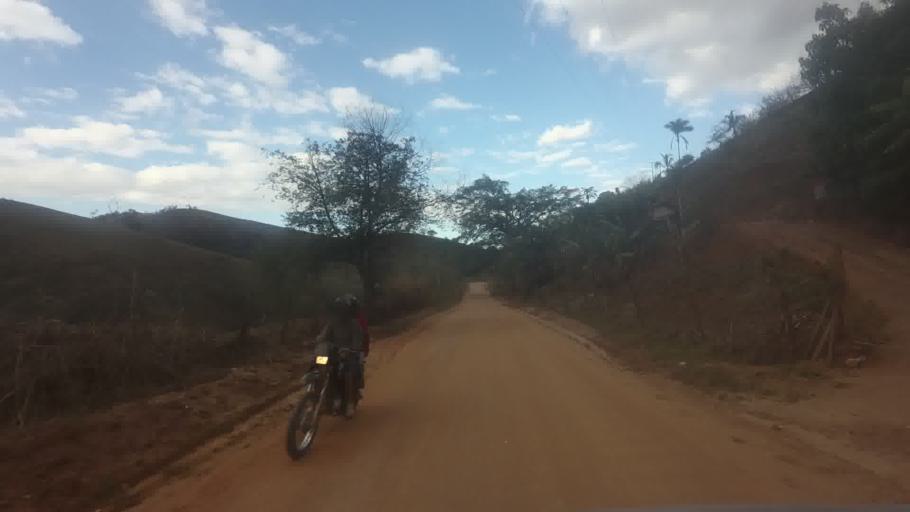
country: BR
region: Espirito Santo
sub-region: Mimoso Do Sul
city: Mimoso do Sul
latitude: -20.9470
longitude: -41.3764
